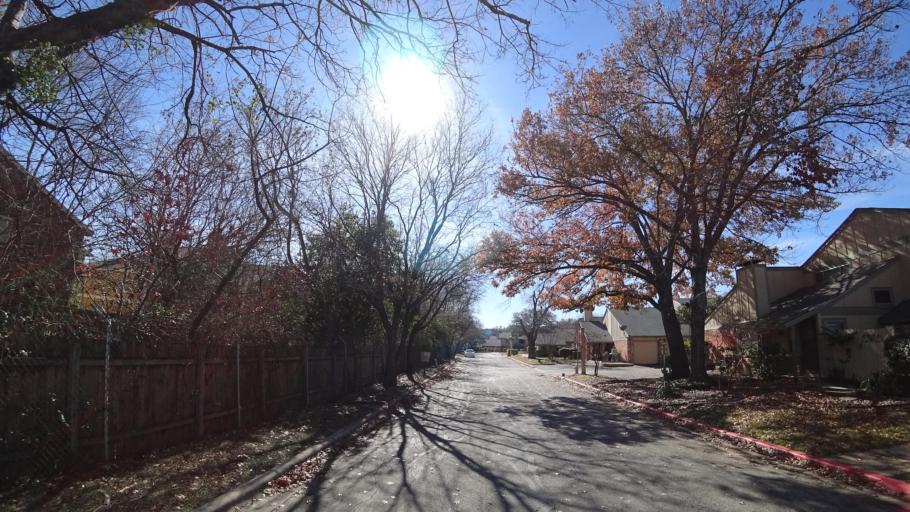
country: US
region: Texas
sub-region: Travis County
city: Wells Branch
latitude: 30.3691
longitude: -97.6967
